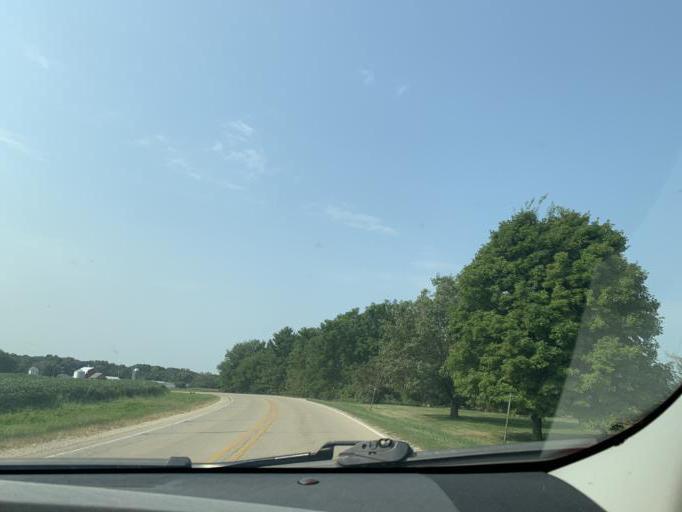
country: US
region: Illinois
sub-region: Whiteside County
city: Sterling
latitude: 41.8221
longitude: -89.7408
